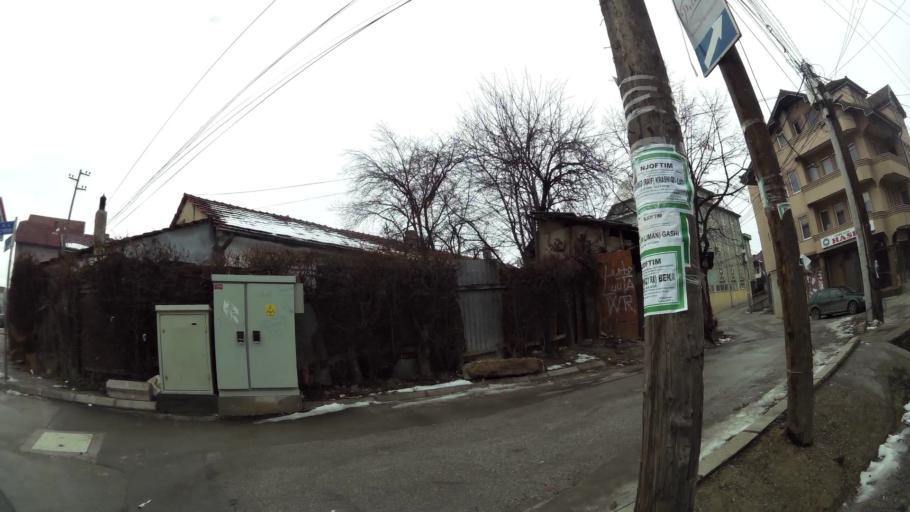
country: XK
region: Pristina
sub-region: Komuna e Prishtines
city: Pristina
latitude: 42.6786
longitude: 21.1669
